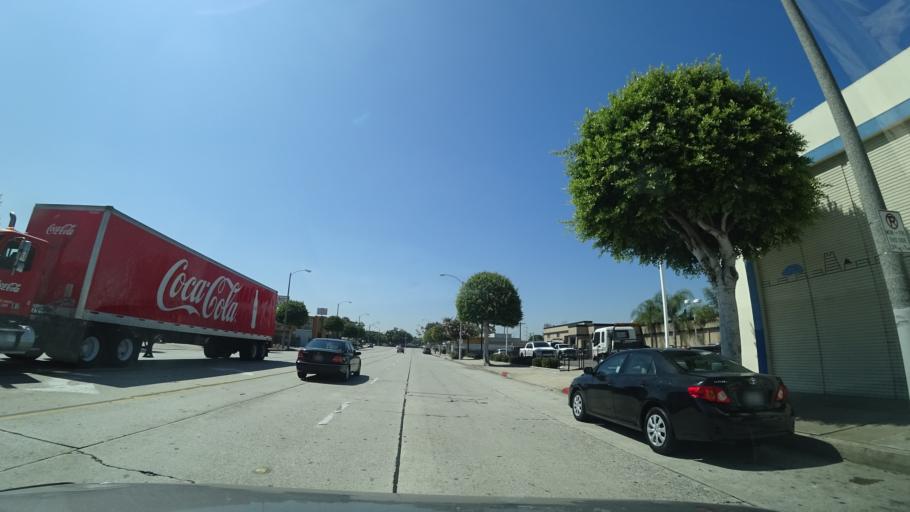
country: US
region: California
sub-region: Los Angeles County
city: Inglewood
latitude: 33.9730
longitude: -118.3577
